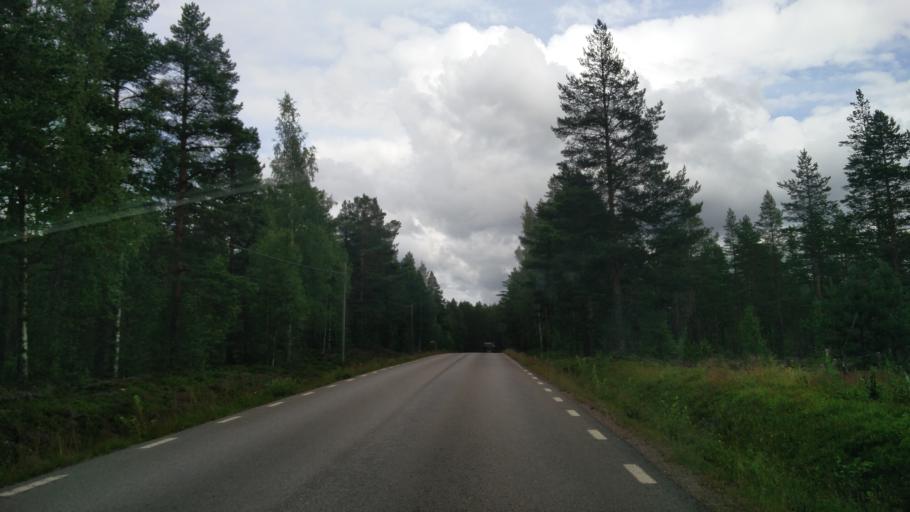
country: NO
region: Hedmark
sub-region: Trysil
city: Innbygda
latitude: 61.1765
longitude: 12.8584
